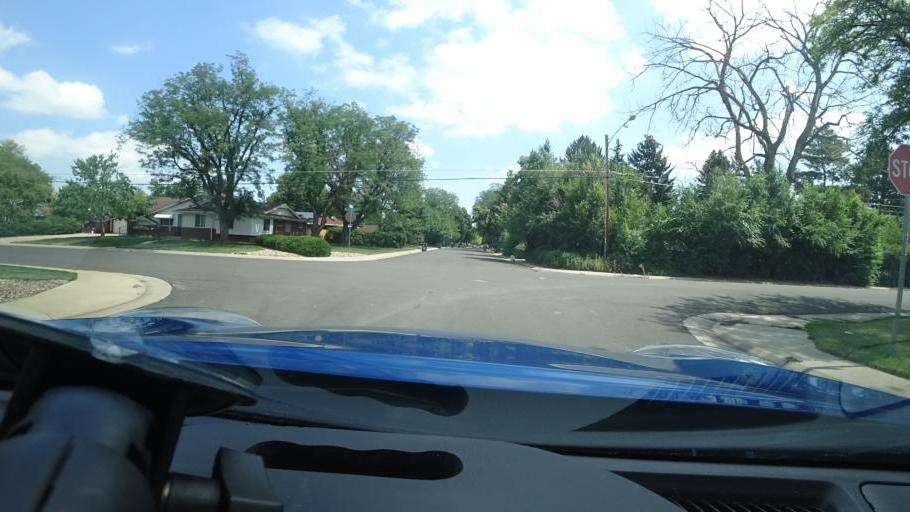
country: US
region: Colorado
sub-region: Adams County
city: Aurora
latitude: 39.7209
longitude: -104.8524
